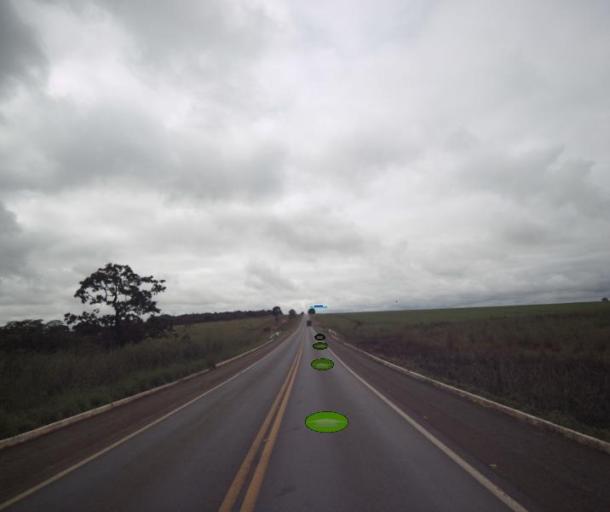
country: BR
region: Goias
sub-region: Uruacu
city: Uruacu
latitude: -14.6575
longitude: -49.1606
